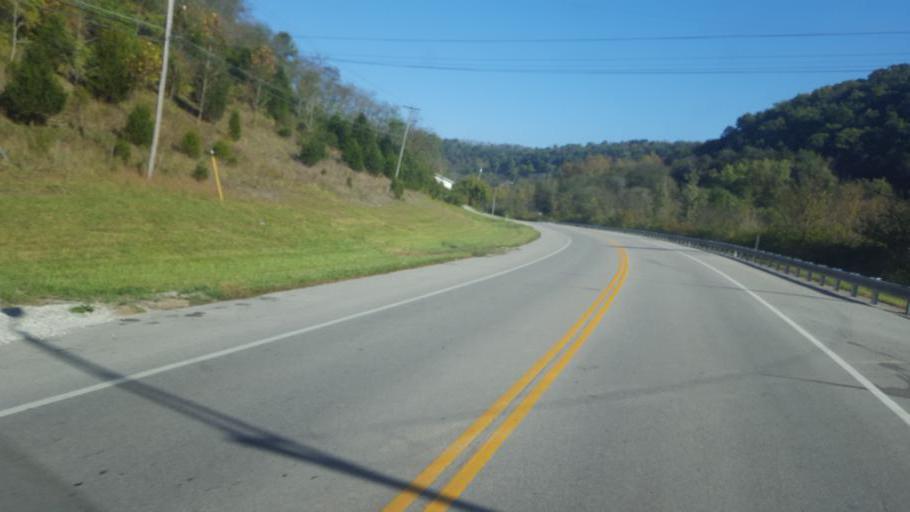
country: US
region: Kentucky
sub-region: Mason County
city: Maysville
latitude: 38.6239
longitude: -83.7516
